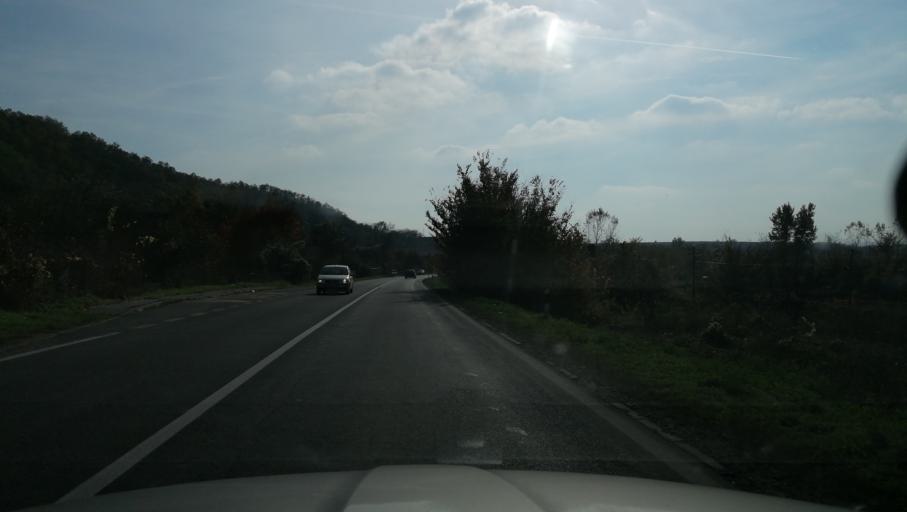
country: RS
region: Central Serbia
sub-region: Rasinski Okrug
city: Krusevac
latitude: 43.6250
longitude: 21.3764
